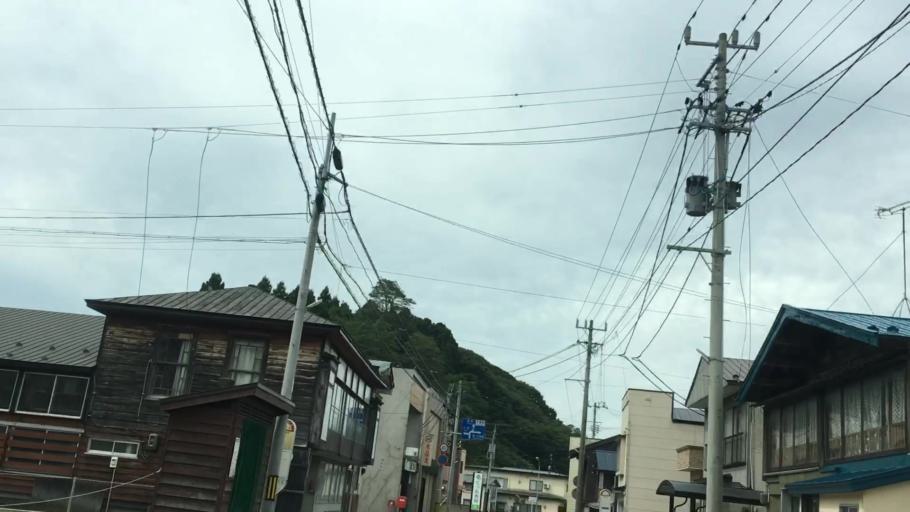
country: JP
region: Aomori
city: Shimokizukuri
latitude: 40.7780
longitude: 140.2142
